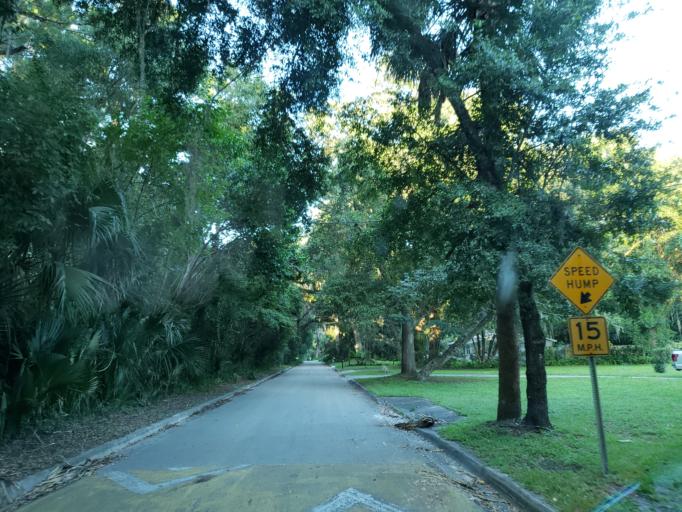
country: US
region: Florida
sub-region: Alachua County
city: Gainesville
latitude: 29.5032
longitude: -82.2851
